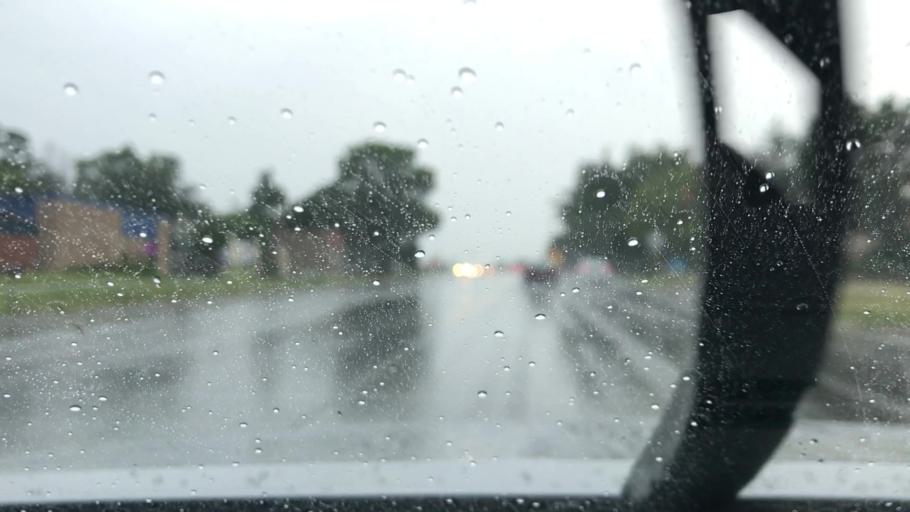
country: US
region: Illinois
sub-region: DuPage County
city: Lisle
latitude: 41.8002
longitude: -88.0871
